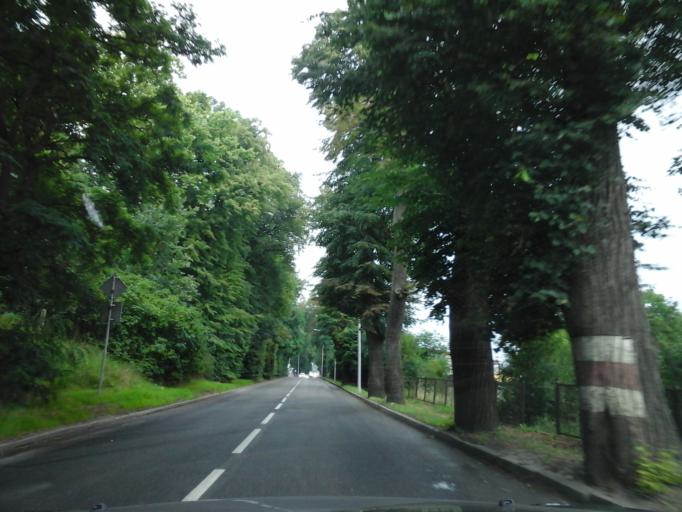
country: PL
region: Lubusz
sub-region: Powiat strzelecko-drezdenecki
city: Drezdenko
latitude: 52.8535
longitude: 15.8309
